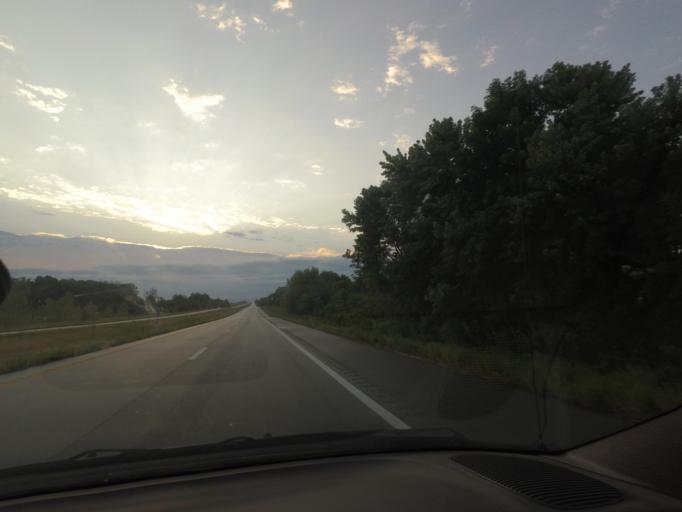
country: US
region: Missouri
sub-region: Shelby County
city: Shelbina
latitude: 39.7333
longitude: -92.2098
